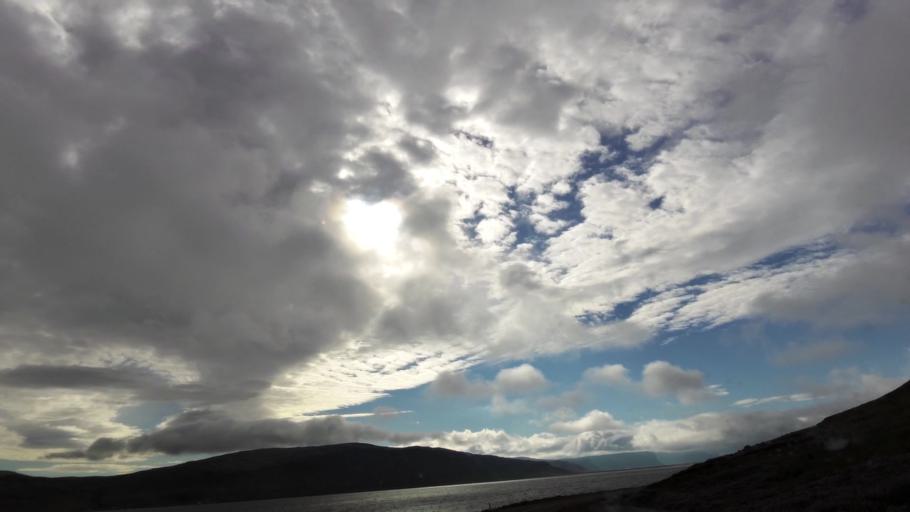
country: IS
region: West
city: Olafsvik
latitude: 65.5436
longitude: -23.8794
